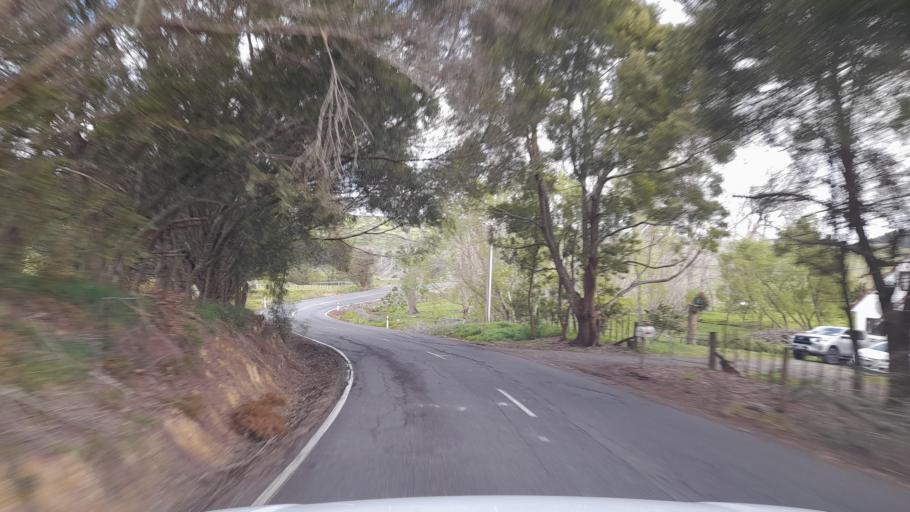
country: NZ
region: Northland
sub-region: Whangarei
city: Maungatapere
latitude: -35.7717
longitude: 174.2452
